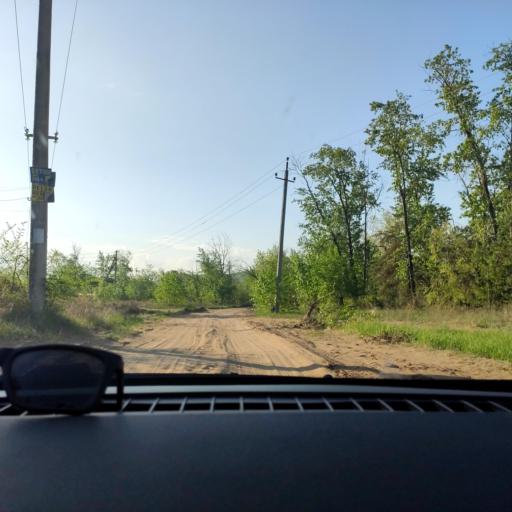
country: RU
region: Samara
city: Volzhskiy
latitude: 53.4340
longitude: 50.1611
